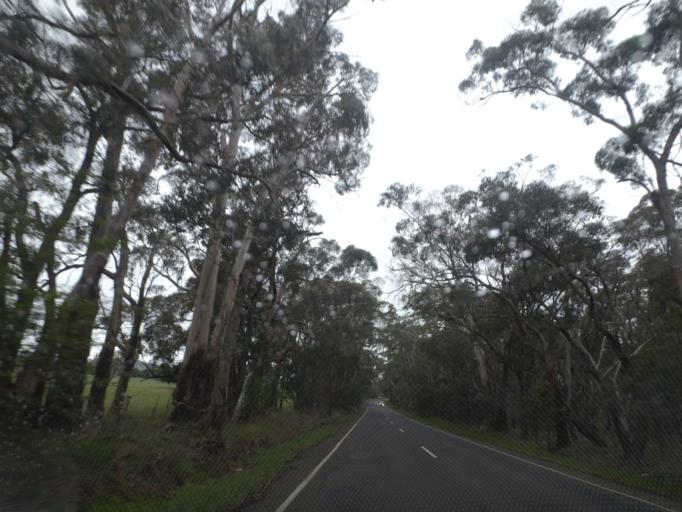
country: AU
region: Victoria
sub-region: Hume
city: Sunbury
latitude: -37.3444
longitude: 144.6883
